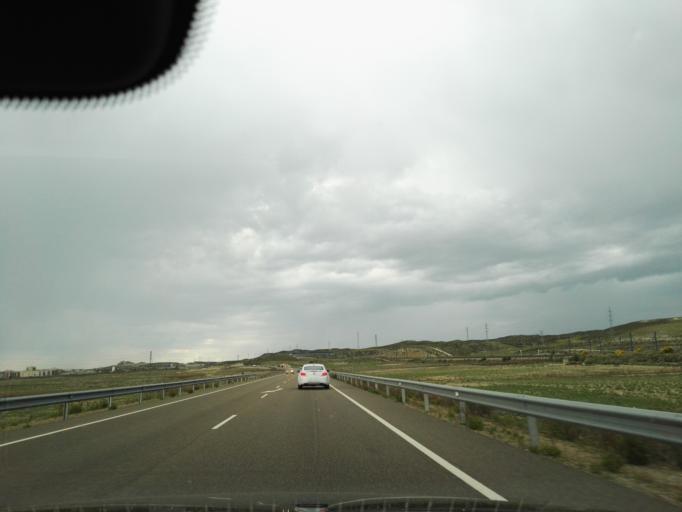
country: ES
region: Aragon
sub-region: Provincia de Zaragoza
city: Montecanal
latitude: 41.6243
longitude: -0.9852
